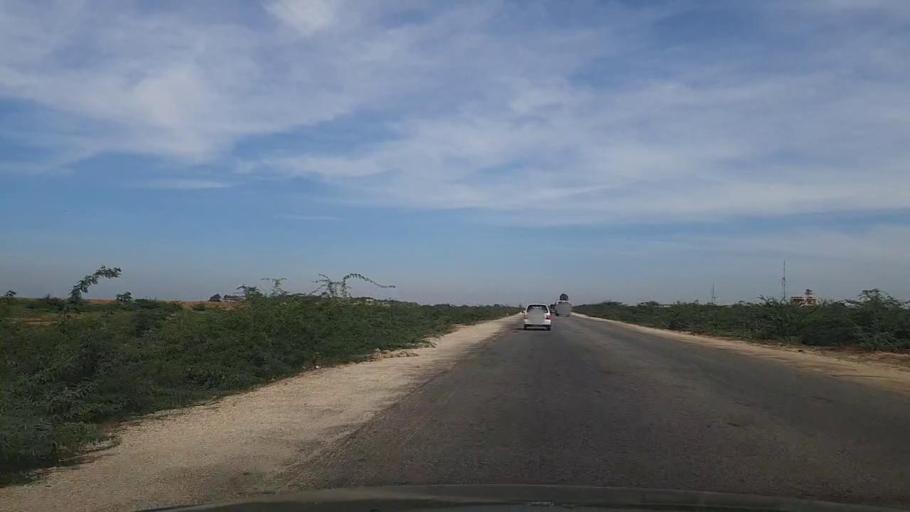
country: PK
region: Sindh
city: Daro Mehar
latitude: 24.8883
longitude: 68.0569
